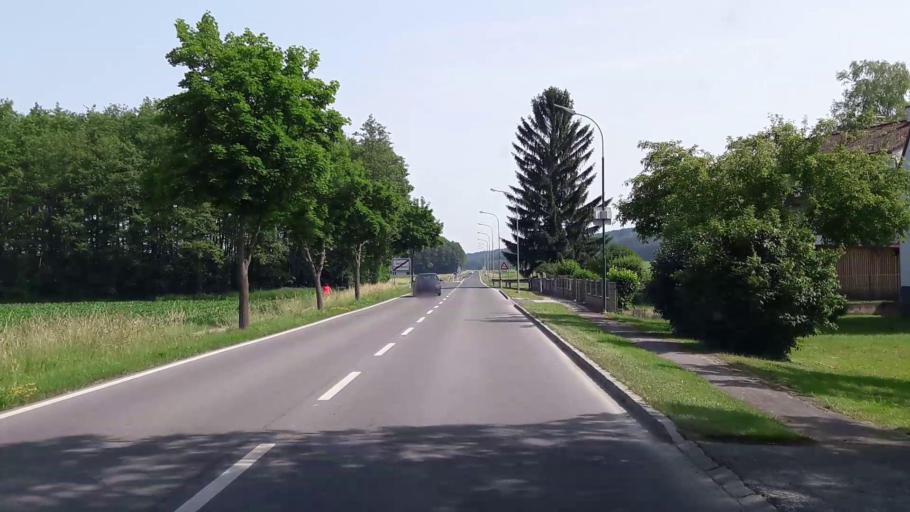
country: AT
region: Burgenland
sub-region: Politischer Bezirk Jennersdorf
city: Deutsch Kaltenbrunn
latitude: 47.0935
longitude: 16.1057
